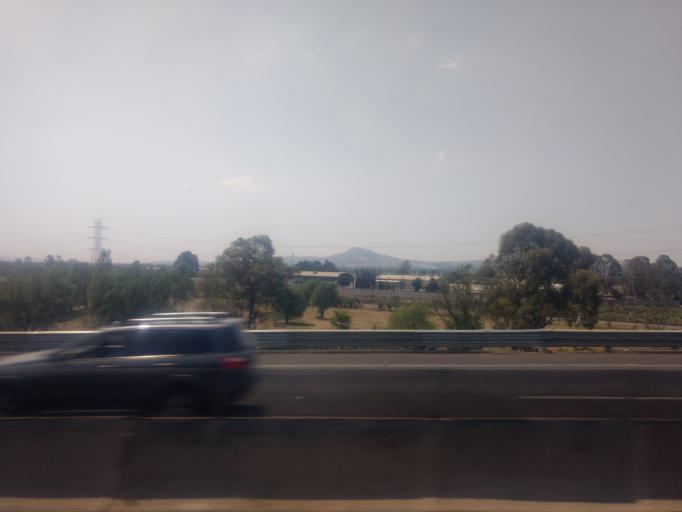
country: MX
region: Morelos
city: San Martin de las Piramides
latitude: 19.6854
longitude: -98.8185
